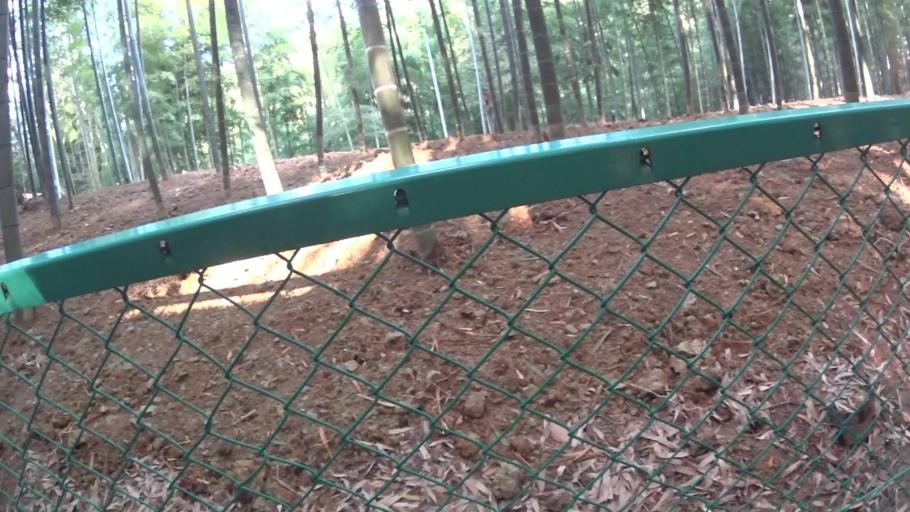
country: JP
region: Kyoto
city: Kyoto
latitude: 34.9663
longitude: 135.7772
